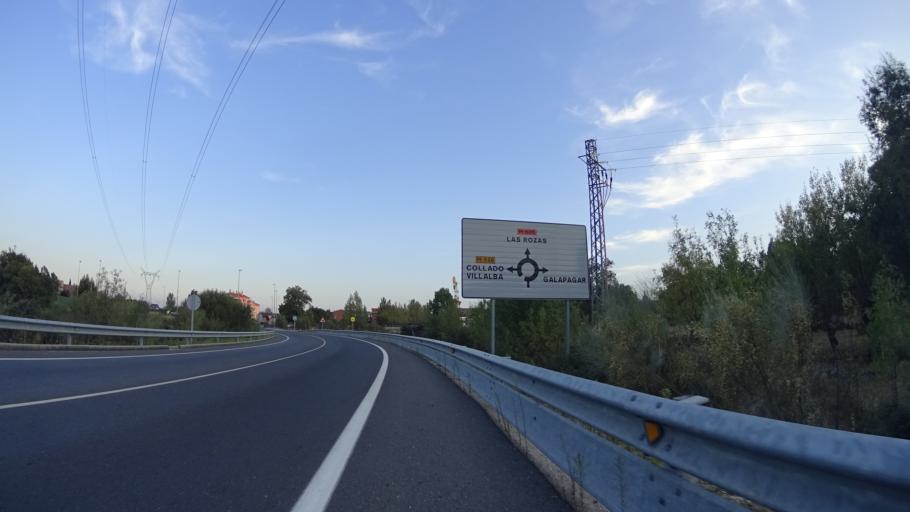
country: ES
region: Madrid
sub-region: Provincia de Madrid
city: Galapagar
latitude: 40.5849
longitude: -4.0018
